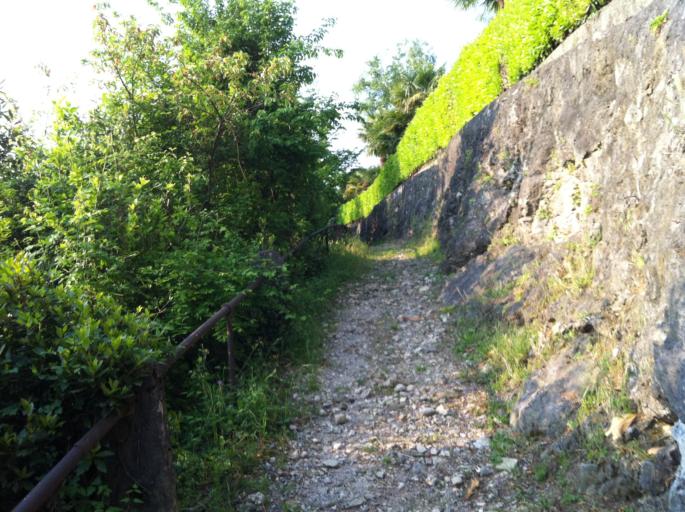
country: IT
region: Lombardy
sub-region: Provincia di Como
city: Menaggio
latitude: 46.0307
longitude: 9.2343
